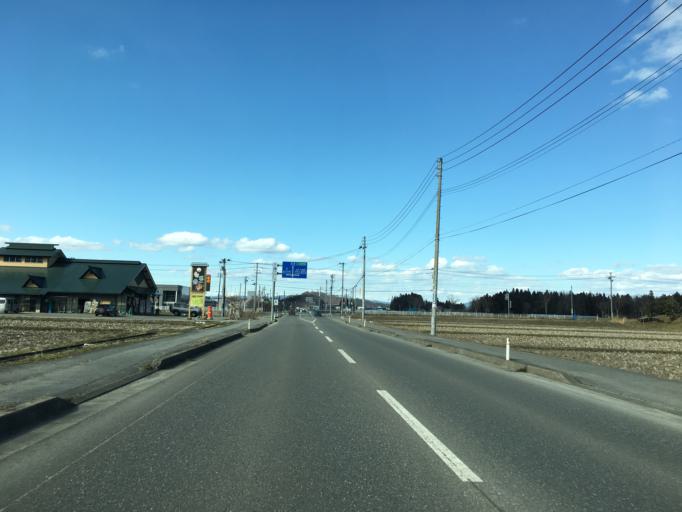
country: JP
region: Yamagata
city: Yonezawa
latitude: 37.9083
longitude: 140.1464
